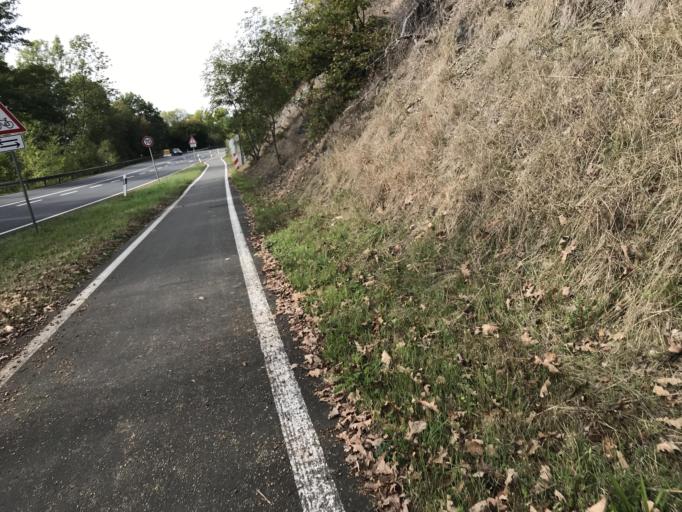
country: DE
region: Hesse
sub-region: Regierungsbezirk Giessen
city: Asslar
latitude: 50.5941
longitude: 8.4371
